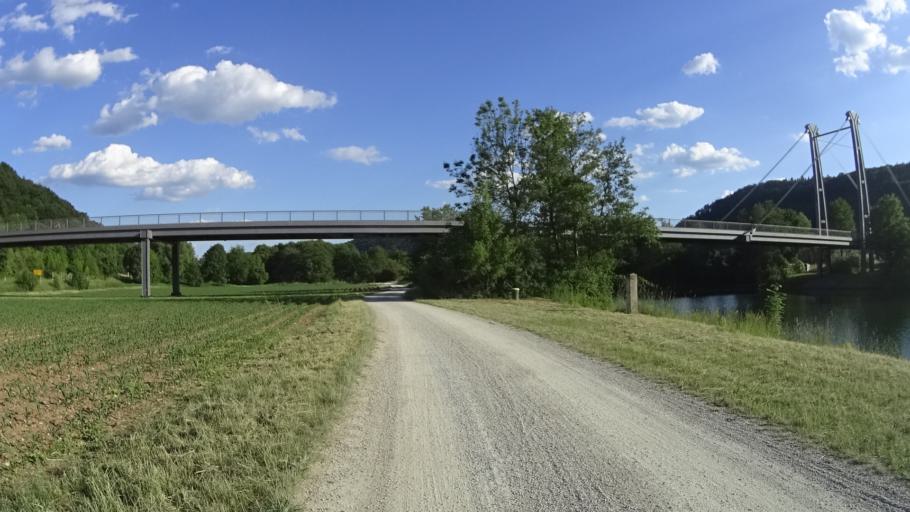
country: DE
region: Bavaria
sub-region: Upper Palatinate
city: Dietfurt
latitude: 48.9943
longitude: 11.6315
